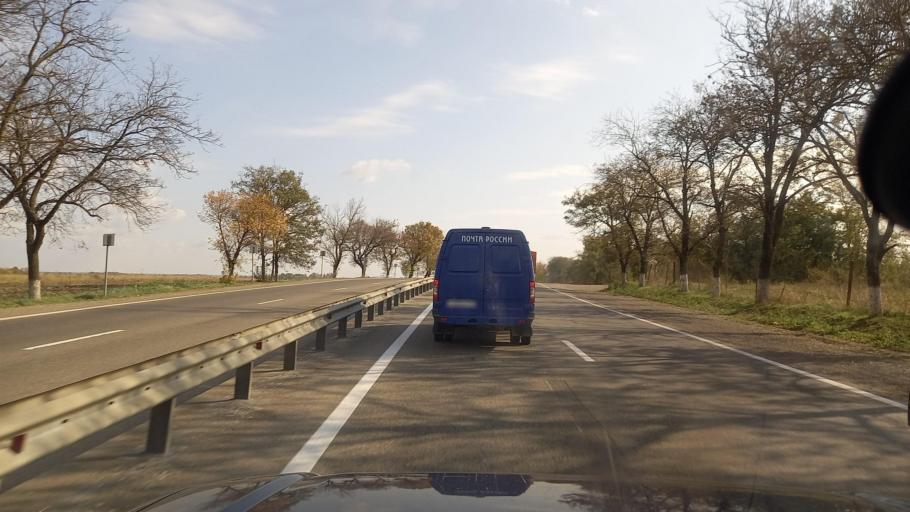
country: RU
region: Krasnodarskiy
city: Akhtyrskiy
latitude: 44.8545
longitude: 38.2547
